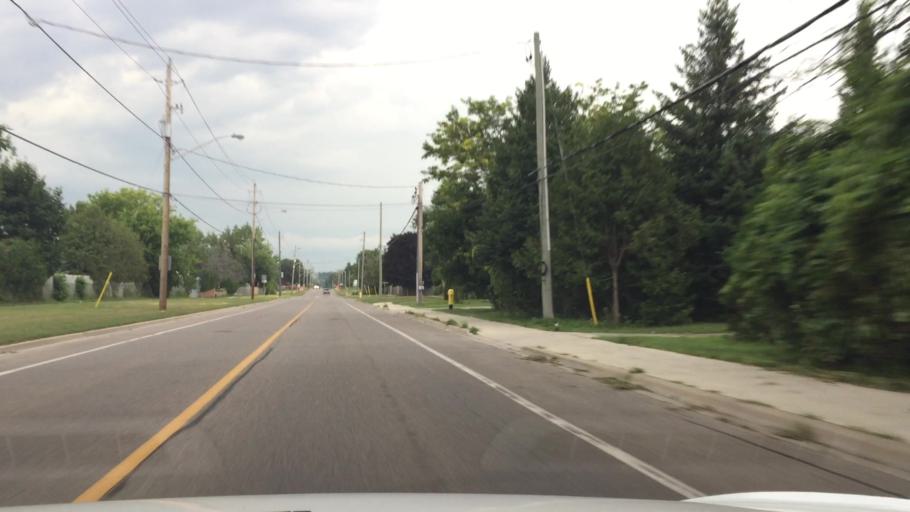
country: CA
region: Ontario
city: Oshawa
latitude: 43.9163
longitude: -78.7906
